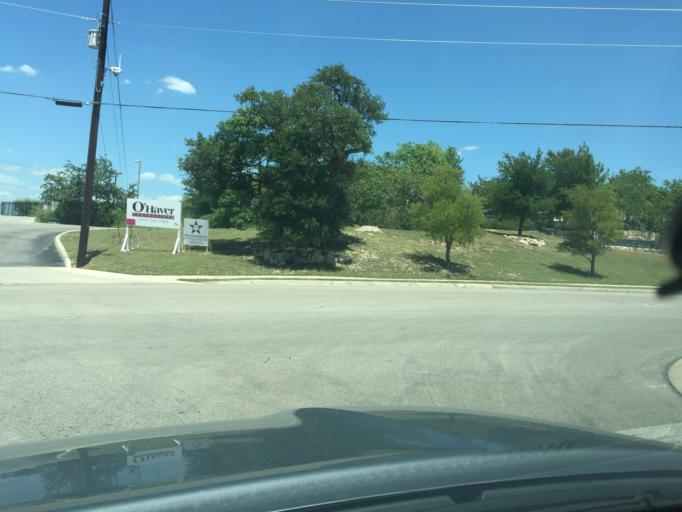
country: US
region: Texas
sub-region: Comal County
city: Bulverde
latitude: 29.7947
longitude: -98.4232
